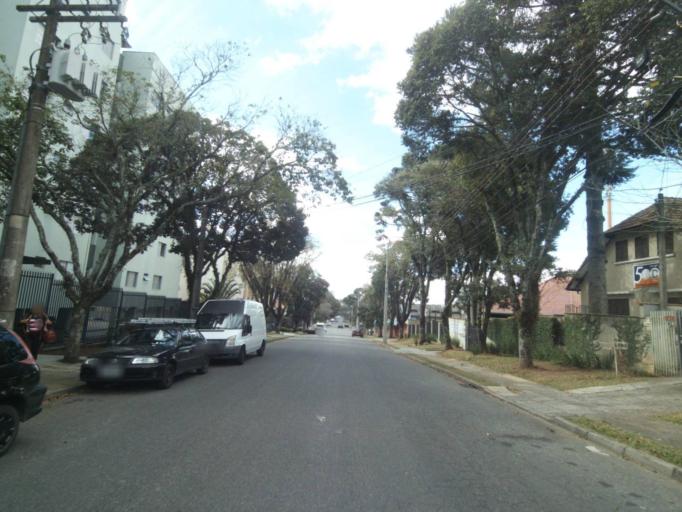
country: BR
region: Parana
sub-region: Curitiba
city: Curitiba
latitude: -25.4660
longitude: -49.2823
